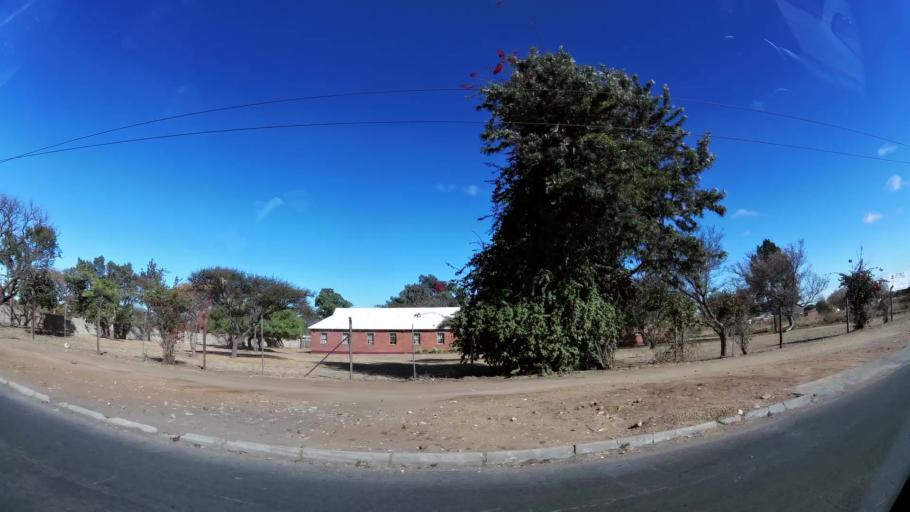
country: ZA
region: Limpopo
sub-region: Capricorn District Municipality
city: Polokwane
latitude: -23.8920
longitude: 29.4475
